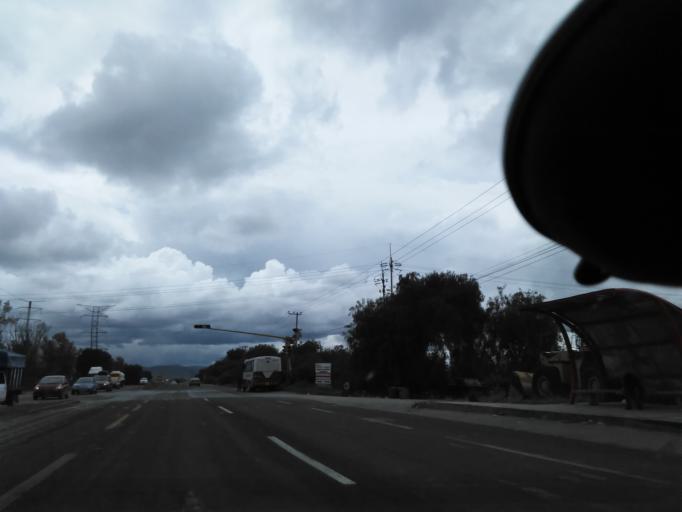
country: MX
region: Hidalgo
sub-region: Tula de Allende
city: Residencial Arboledas
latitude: 20.0603
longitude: -99.2859
